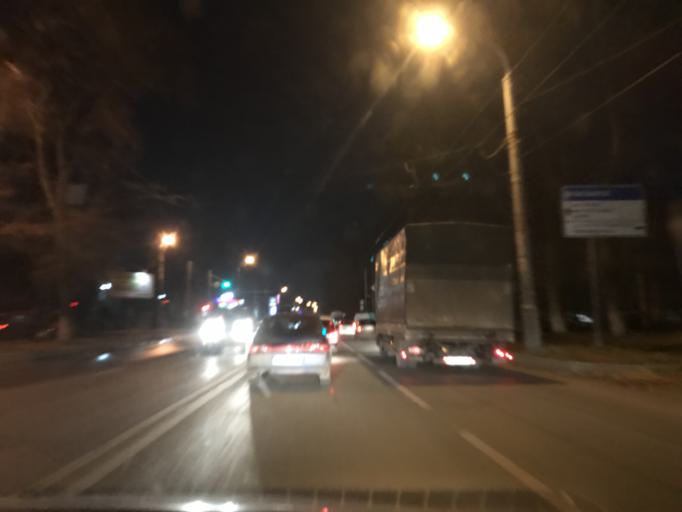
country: RU
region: Rostov
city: Kalinin
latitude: 47.2026
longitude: 39.6135
